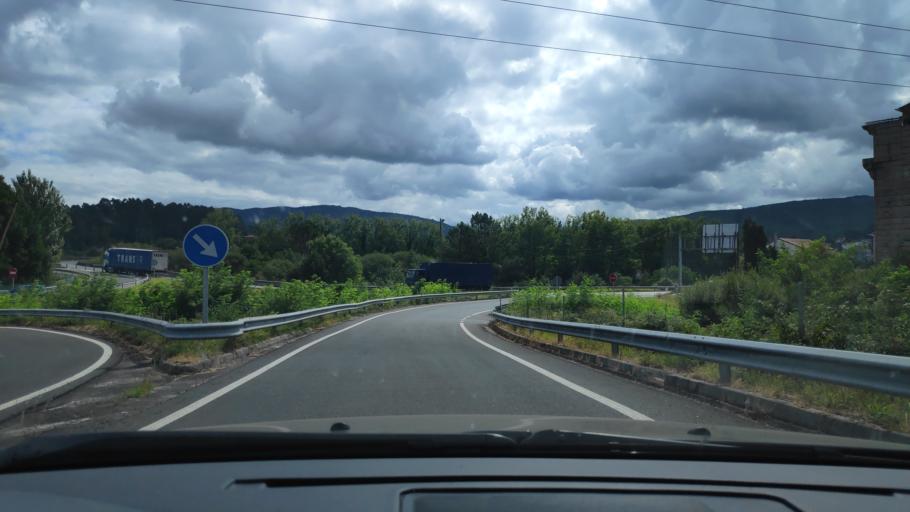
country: ES
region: Galicia
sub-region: Provincia da Coruna
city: Padron
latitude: 42.7308
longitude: -8.6588
